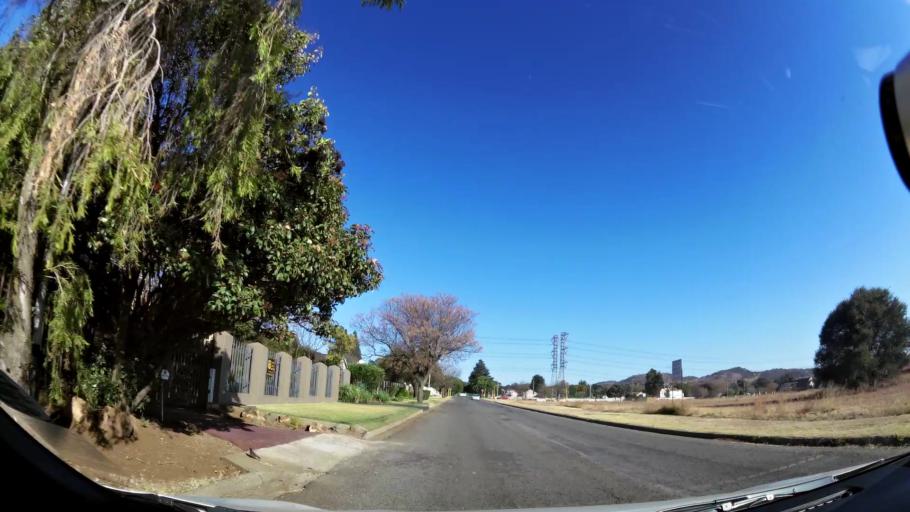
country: ZA
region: Gauteng
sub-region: Ekurhuleni Metropolitan Municipality
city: Germiston
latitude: -26.2817
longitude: 28.1122
